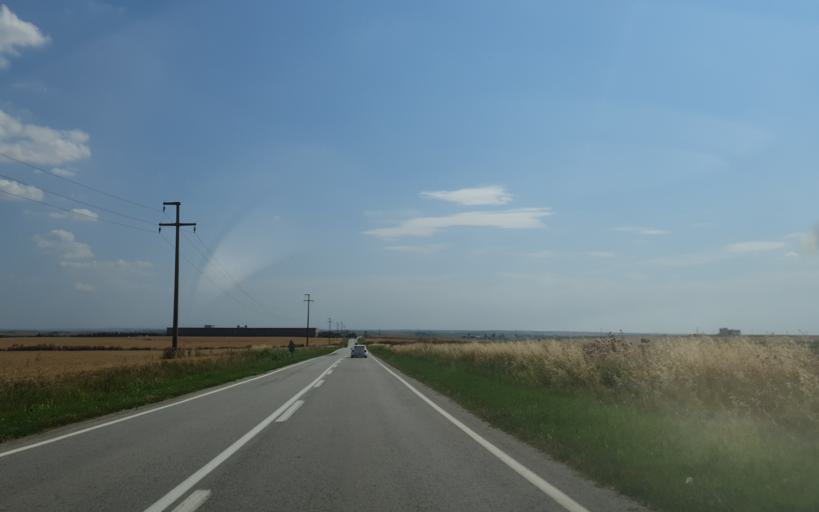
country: TR
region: Kirklareli
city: Buyukkaristiran
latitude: 41.3266
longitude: 27.5284
